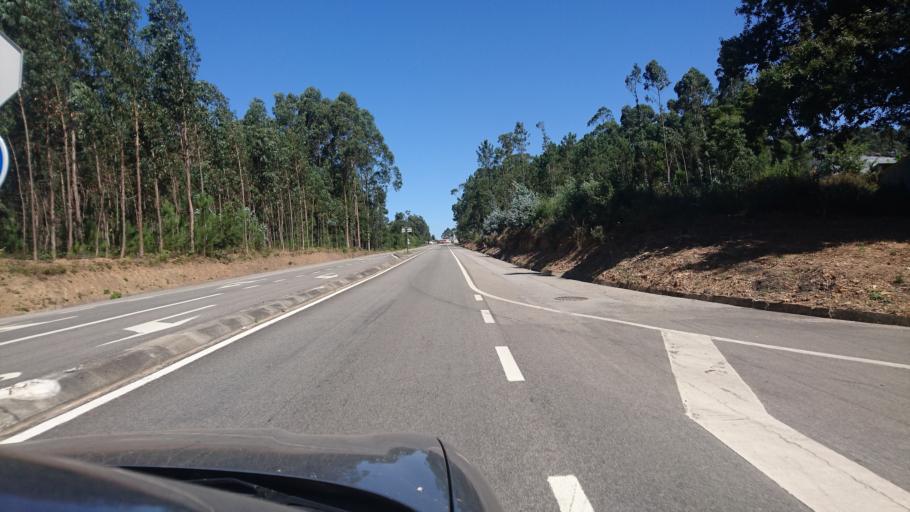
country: PT
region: Aveiro
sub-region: Santa Maria da Feira
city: Rio Meao
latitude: 40.9531
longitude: -8.5866
